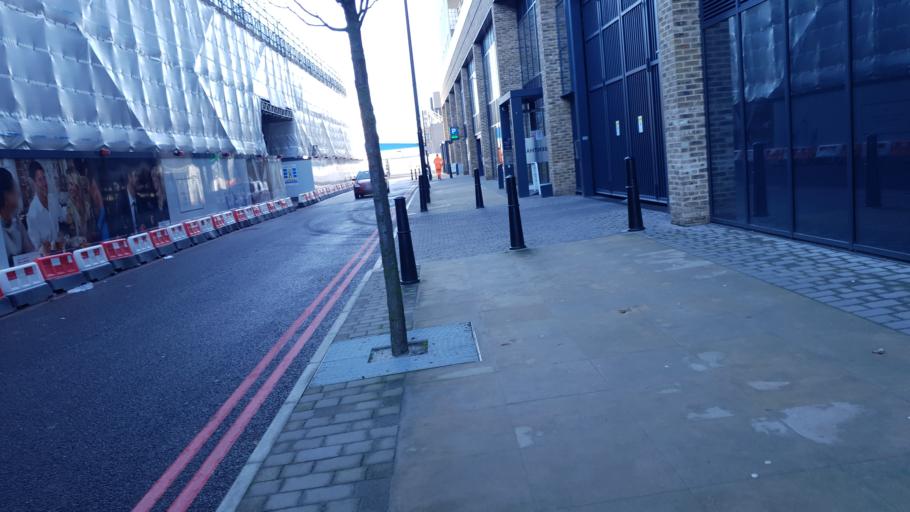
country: GB
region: England
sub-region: Greater London
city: Woolwich
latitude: 51.4918
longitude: 0.0721
